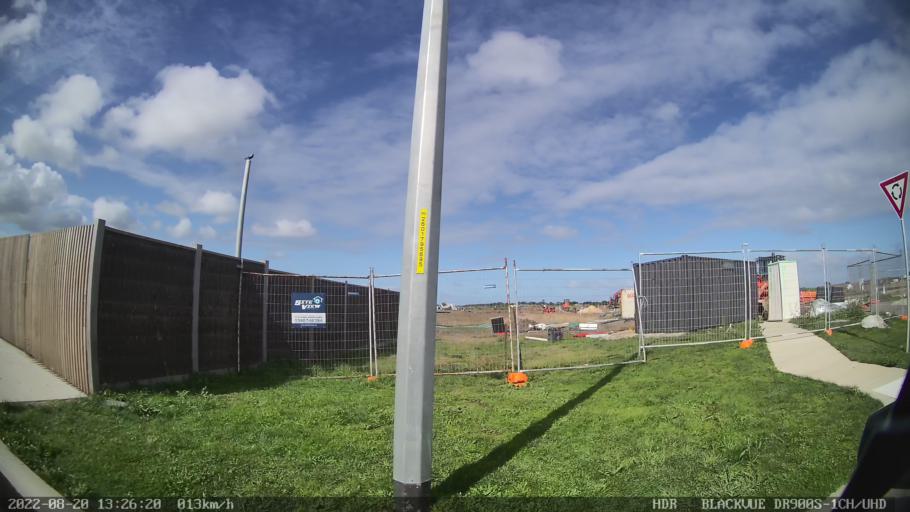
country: AU
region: Victoria
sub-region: Bass Coast
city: North Wonthaggi
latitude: -38.5963
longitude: 145.6132
